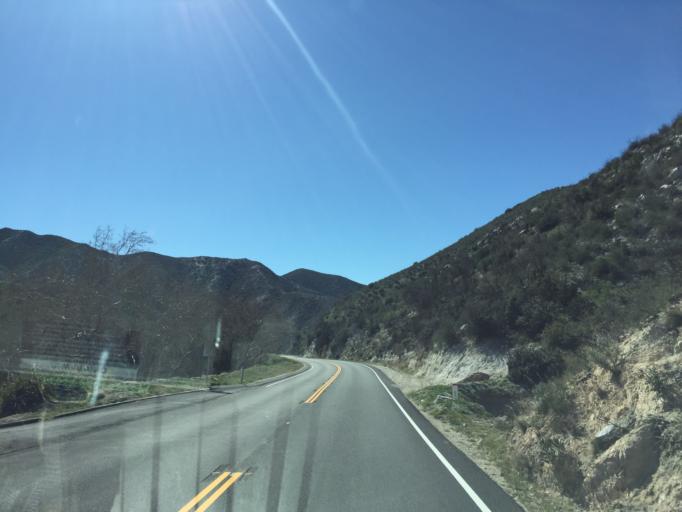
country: US
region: California
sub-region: Los Angeles County
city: Acton
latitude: 34.3431
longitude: -118.1108
